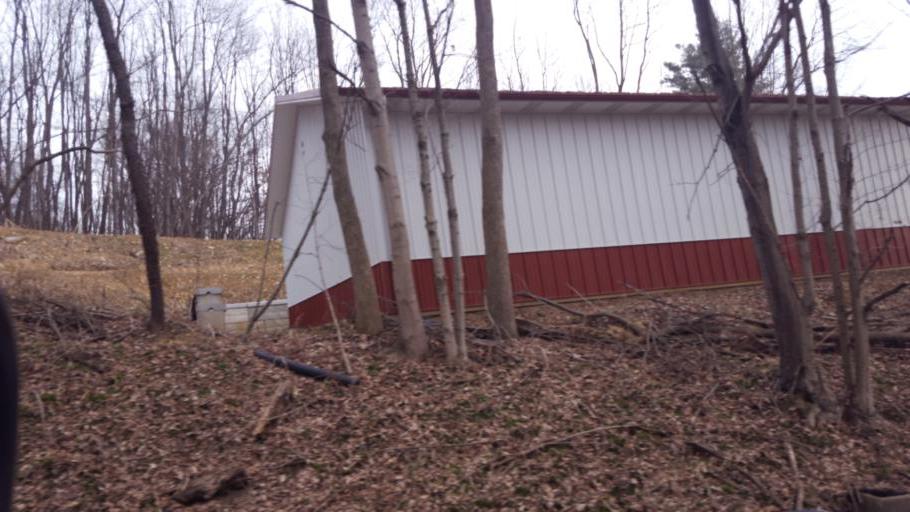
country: US
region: Ohio
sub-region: Knox County
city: Danville
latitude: 40.5306
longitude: -82.3065
